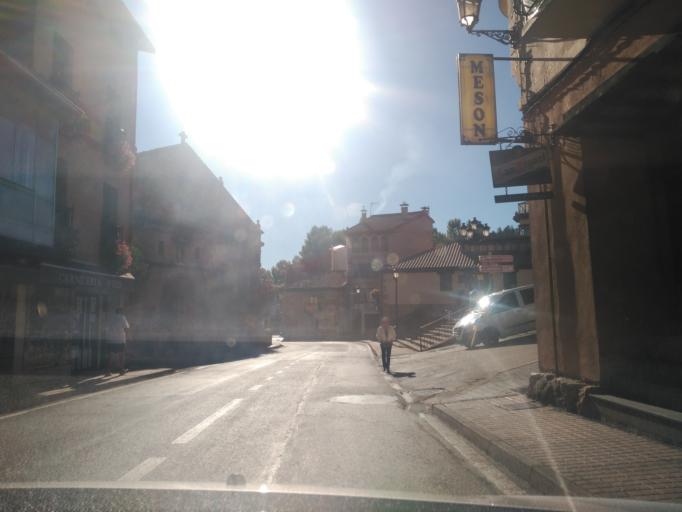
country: ES
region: Castille and Leon
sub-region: Provincia de Soria
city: San Leonardo de Yague
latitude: 41.8293
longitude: -3.0672
